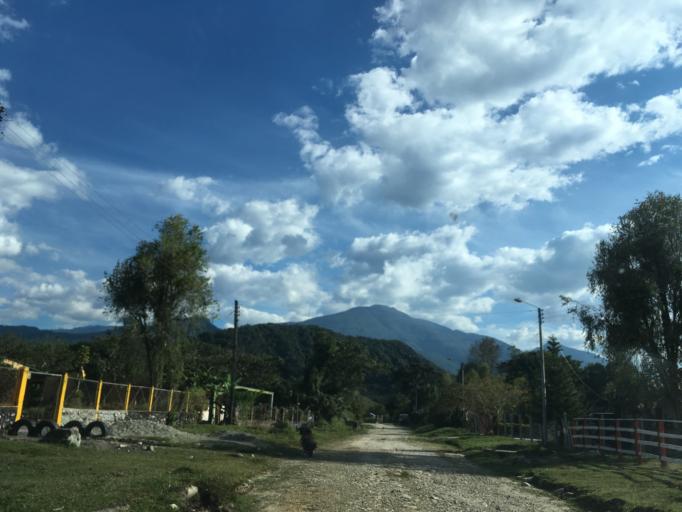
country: CO
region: Santander
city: Oiba
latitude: 6.1056
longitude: -73.1970
